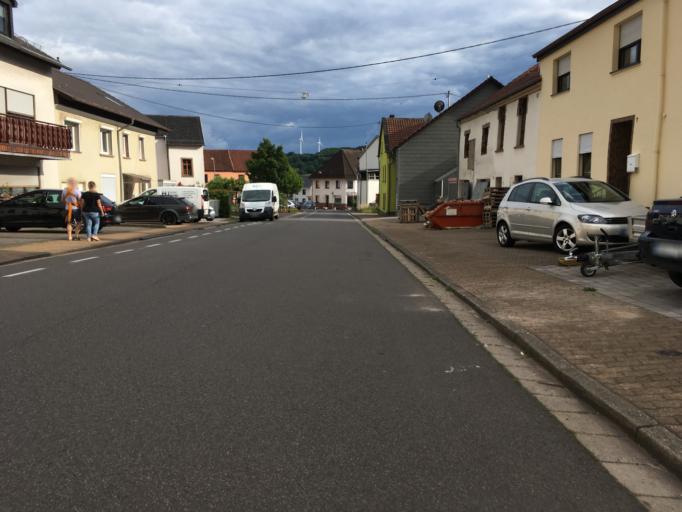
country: DE
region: Saarland
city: Losheim
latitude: 49.5125
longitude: 6.7464
